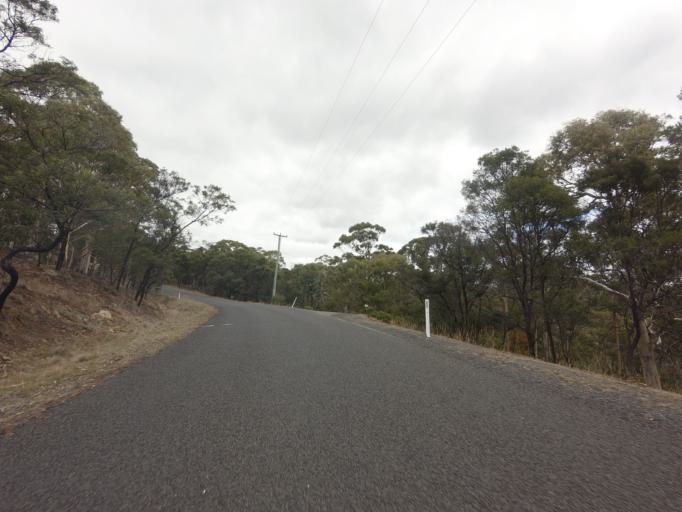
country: AU
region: Tasmania
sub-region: Clarence
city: Cambridge
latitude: -42.7888
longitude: 147.3999
